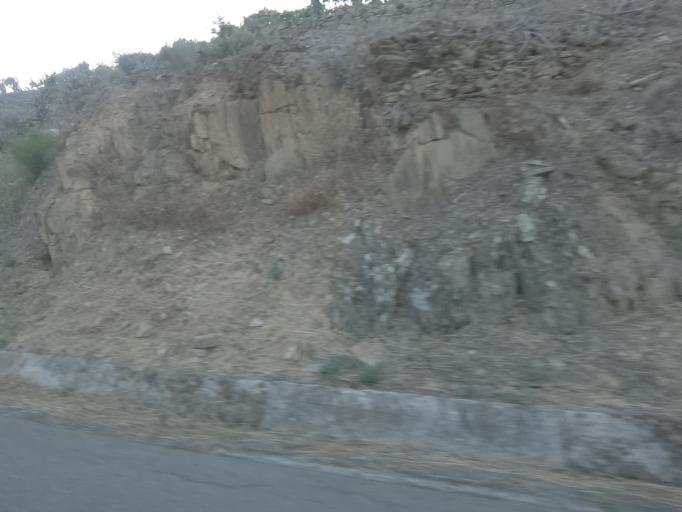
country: PT
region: Viseu
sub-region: Armamar
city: Armamar
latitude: 41.1937
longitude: -7.6868
